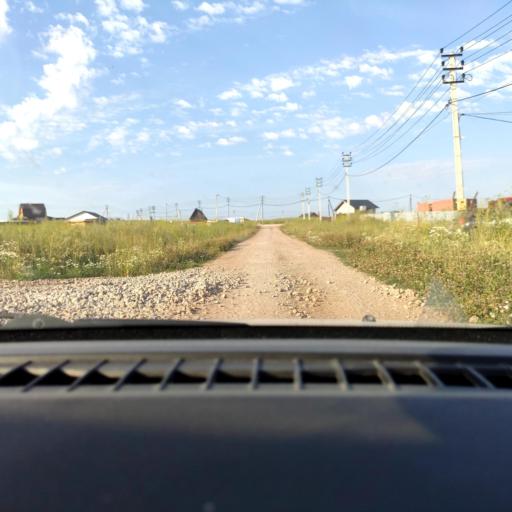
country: RU
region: Perm
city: Ferma
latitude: 57.9503
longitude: 56.3502
